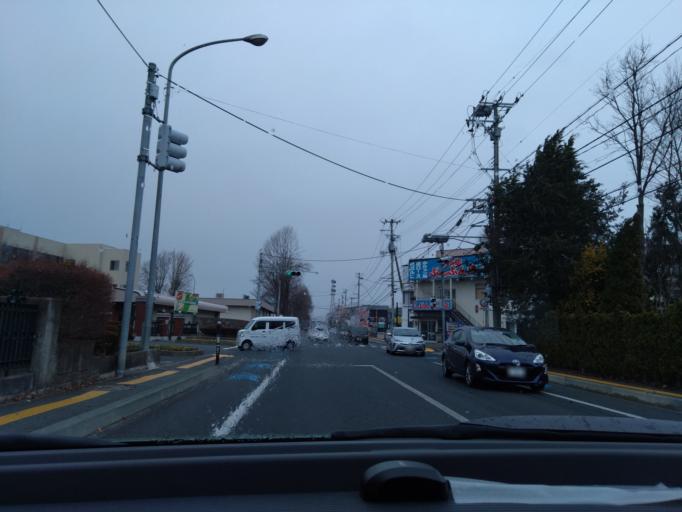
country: JP
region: Iwate
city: Morioka-shi
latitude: 39.7154
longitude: 141.1395
